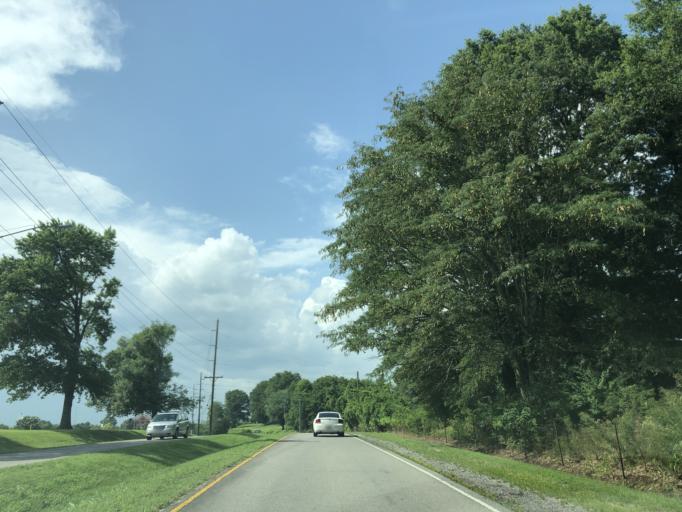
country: US
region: Tennessee
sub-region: Davidson County
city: Lakewood
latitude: 36.1875
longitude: -86.6861
